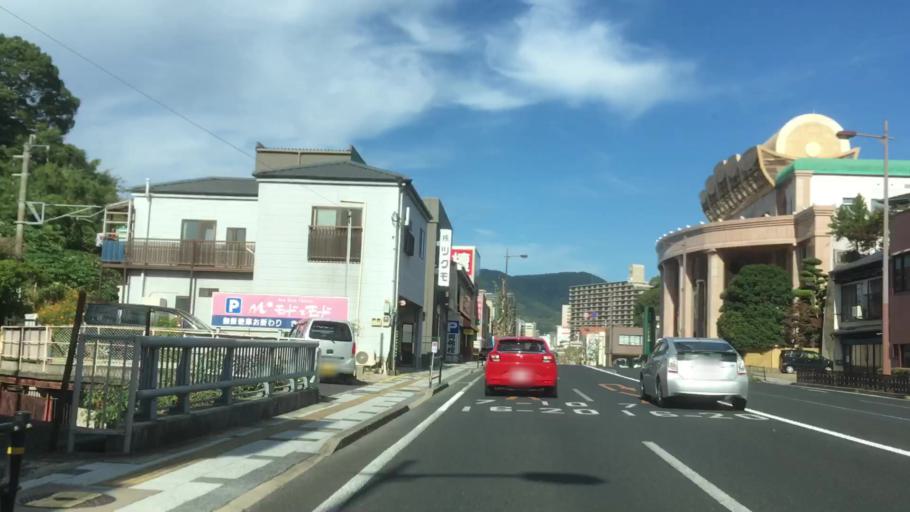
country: JP
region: Nagasaki
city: Sasebo
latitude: 33.1591
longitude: 129.7335
